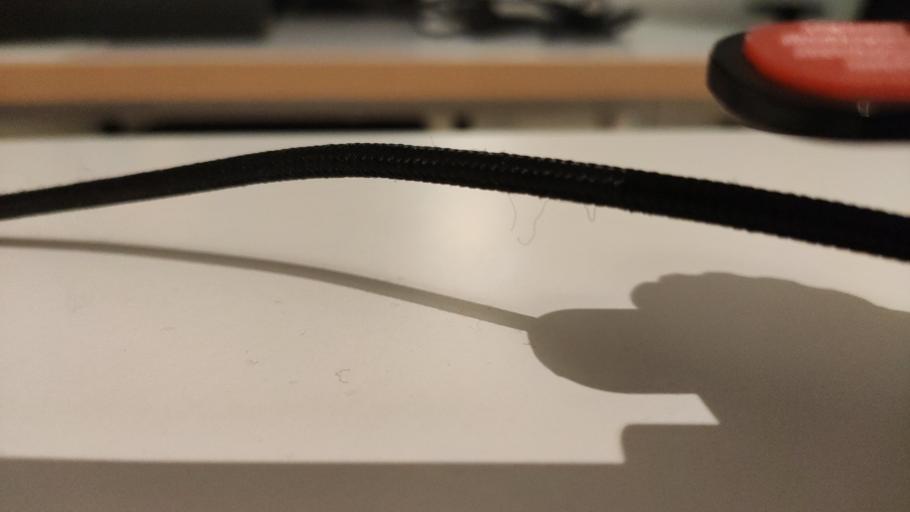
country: RU
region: Moskovskaya
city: Novosin'kovo
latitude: 56.4037
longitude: 37.2483
